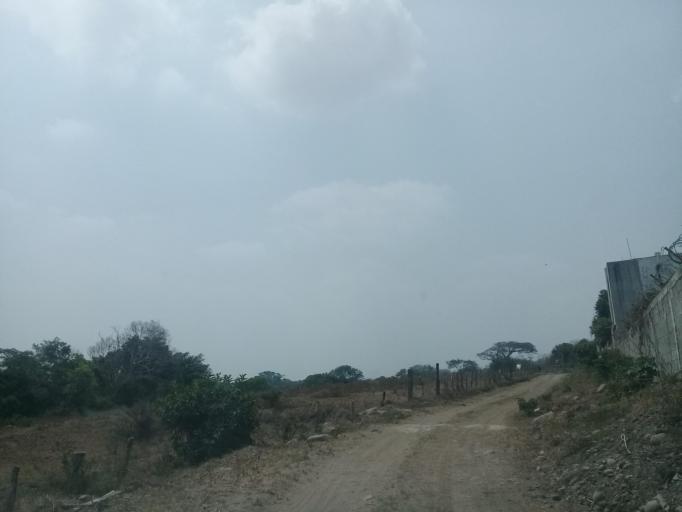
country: MX
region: Veracruz
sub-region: Veracruz
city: Fraccionamiento Geovillas los Pinos
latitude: 19.2324
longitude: -96.2410
